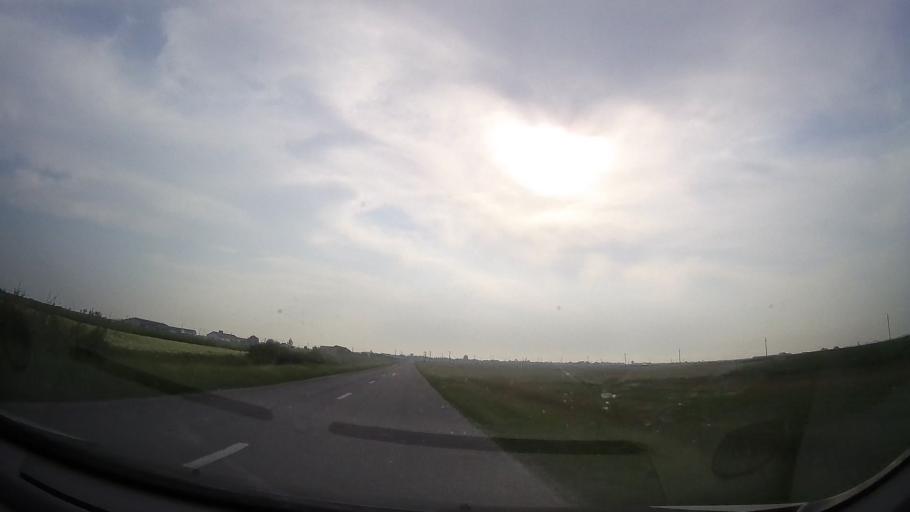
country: RO
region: Timis
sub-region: Comuna Foeni
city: Foeni
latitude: 45.4928
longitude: 20.8503
